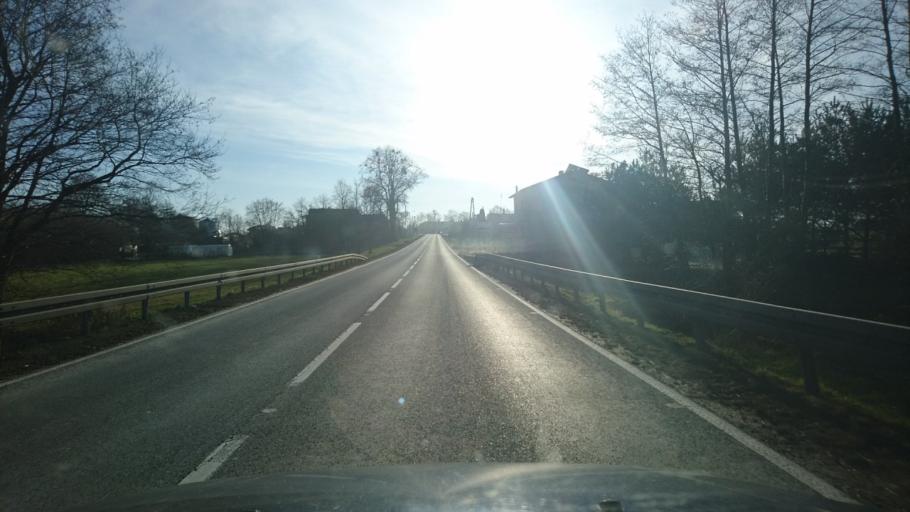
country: PL
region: Opole Voivodeship
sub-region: Powiat oleski
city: Dalachow
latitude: 51.0466
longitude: 18.5972
